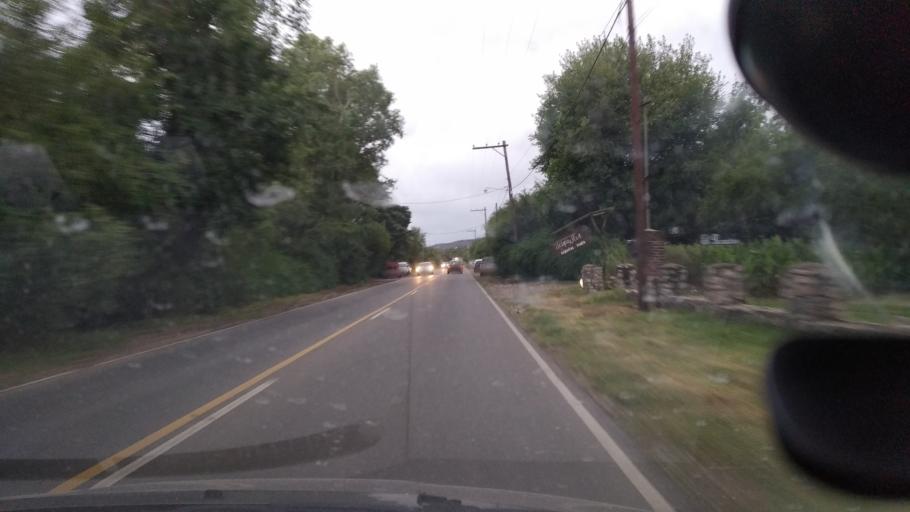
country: AR
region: Cordoba
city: Villa Las Rosas
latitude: -31.9344
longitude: -65.0401
